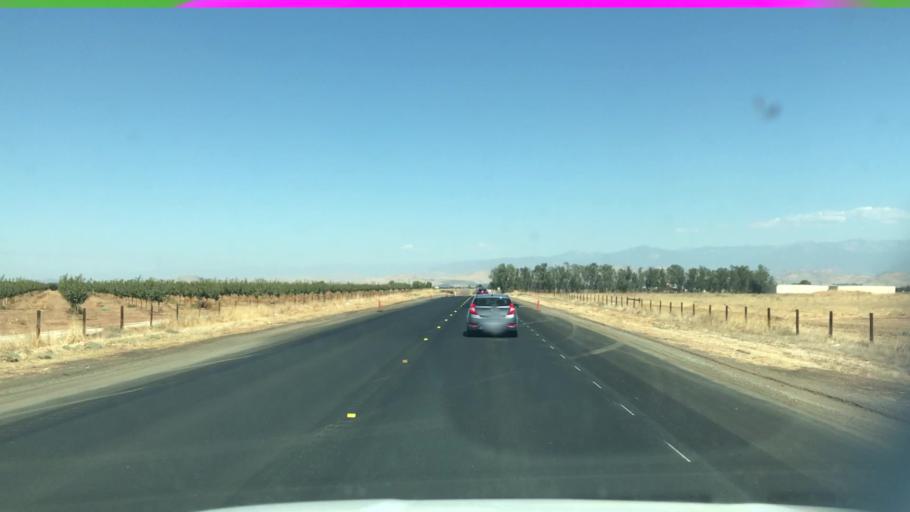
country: US
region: California
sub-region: Tulare County
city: Terra Bella
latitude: 35.9866
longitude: -119.0509
